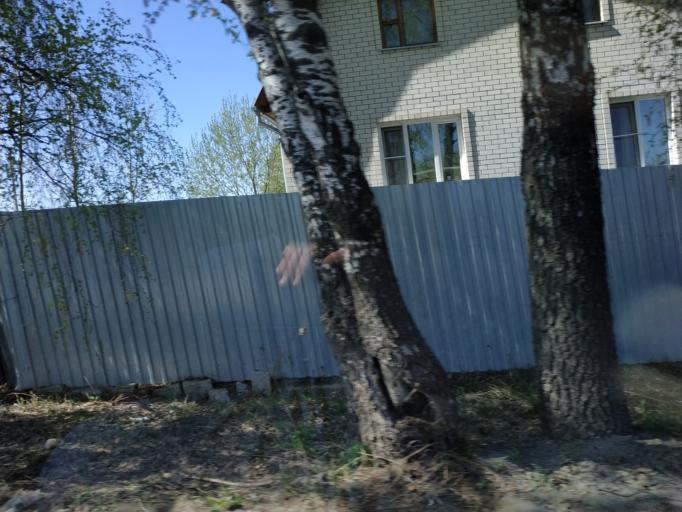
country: RU
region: Moskovskaya
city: Malyshevo
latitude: 55.4739
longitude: 38.3947
